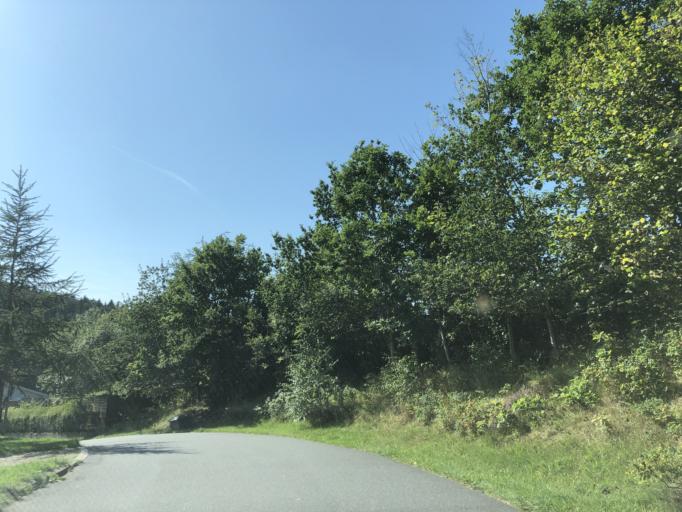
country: DK
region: Central Jutland
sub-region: Silkeborg Kommune
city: Silkeborg
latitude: 56.1923
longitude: 9.5877
